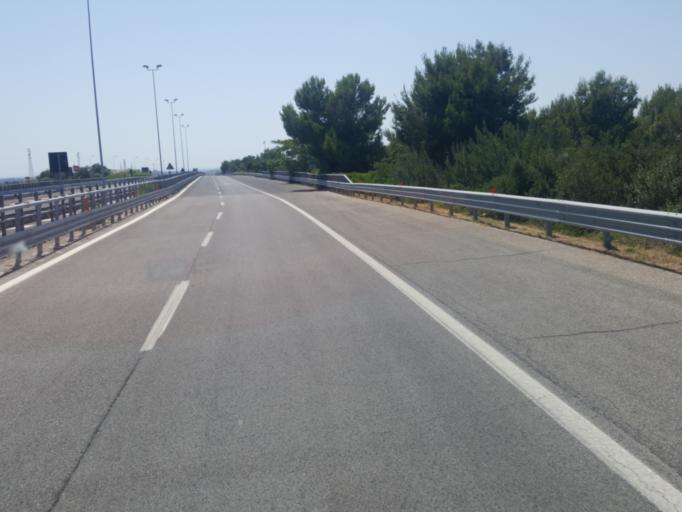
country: IT
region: Apulia
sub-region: Provincia di Taranto
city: Massafra
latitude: 40.5978
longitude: 17.0843
